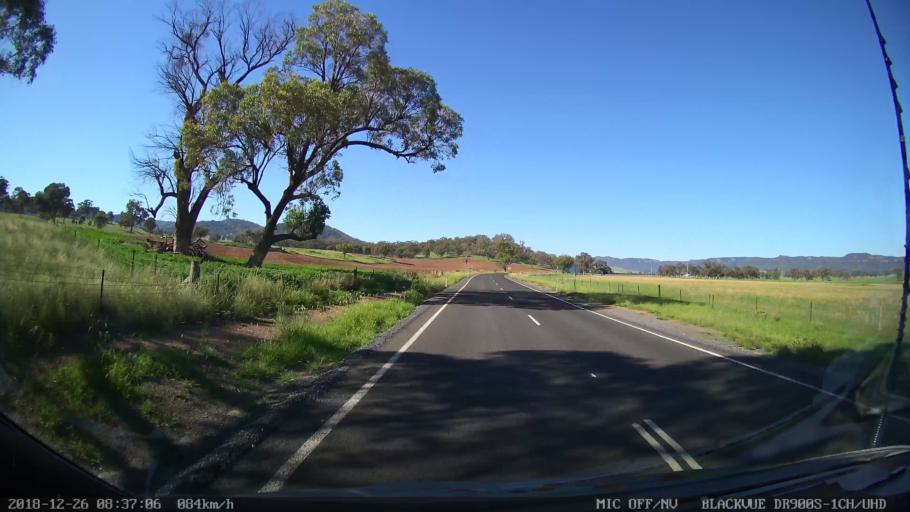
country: AU
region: New South Wales
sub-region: Upper Hunter Shire
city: Merriwa
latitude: -32.4289
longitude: 150.0932
